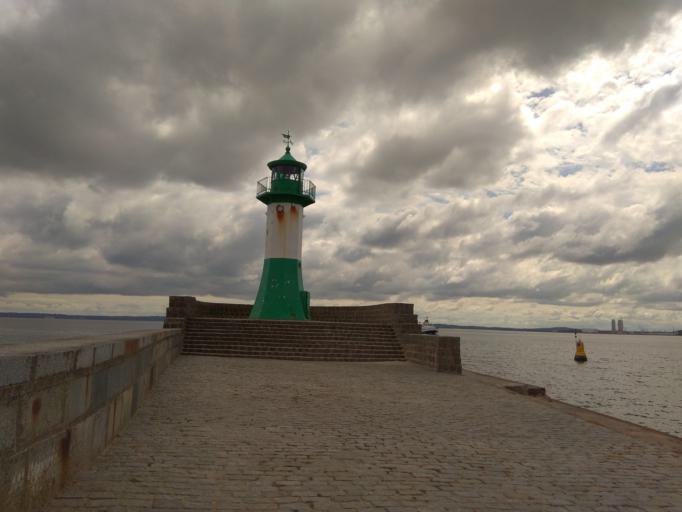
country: DE
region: Mecklenburg-Vorpommern
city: Sassnitz
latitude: 54.5064
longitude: 13.6373
